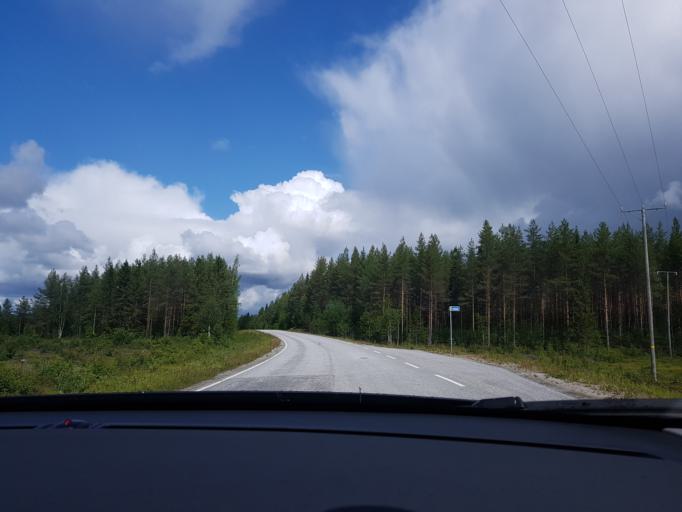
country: FI
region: Kainuu
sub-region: Kehys-Kainuu
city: Kuhmo
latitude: 64.4264
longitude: 29.4989
